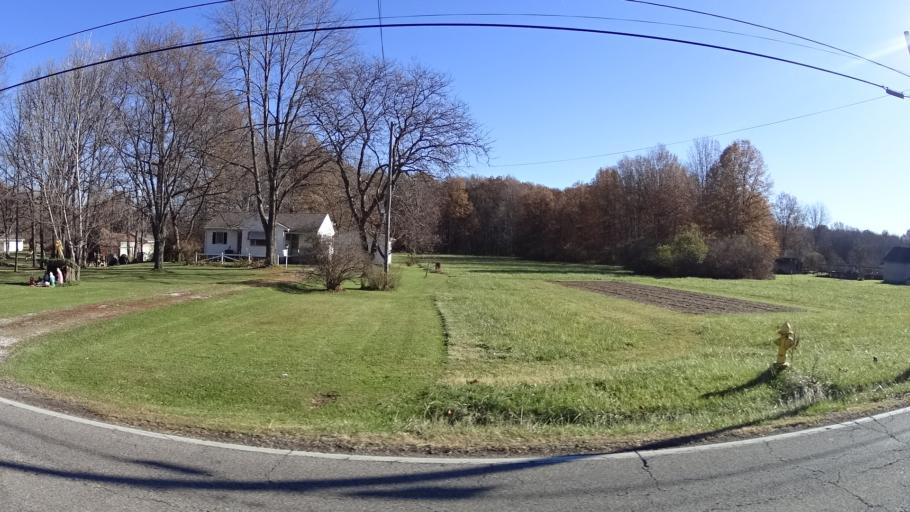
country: US
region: Ohio
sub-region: Lorain County
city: Elyria
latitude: 41.3850
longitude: -82.1500
